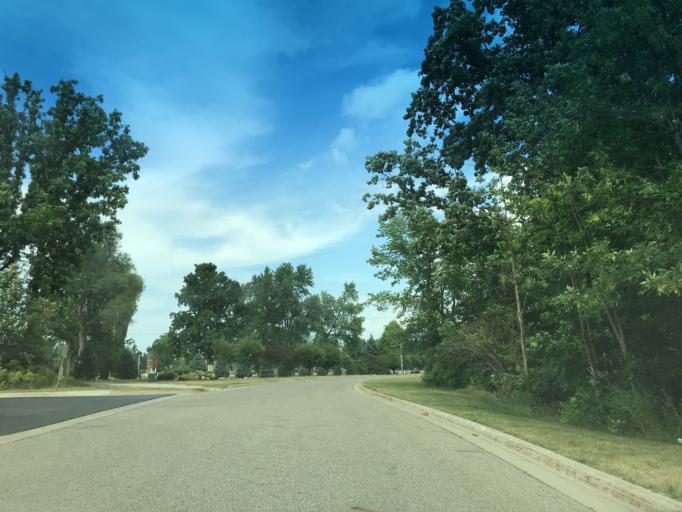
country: US
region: Michigan
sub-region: Eaton County
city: Waverly
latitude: 42.7174
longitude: -84.6281
